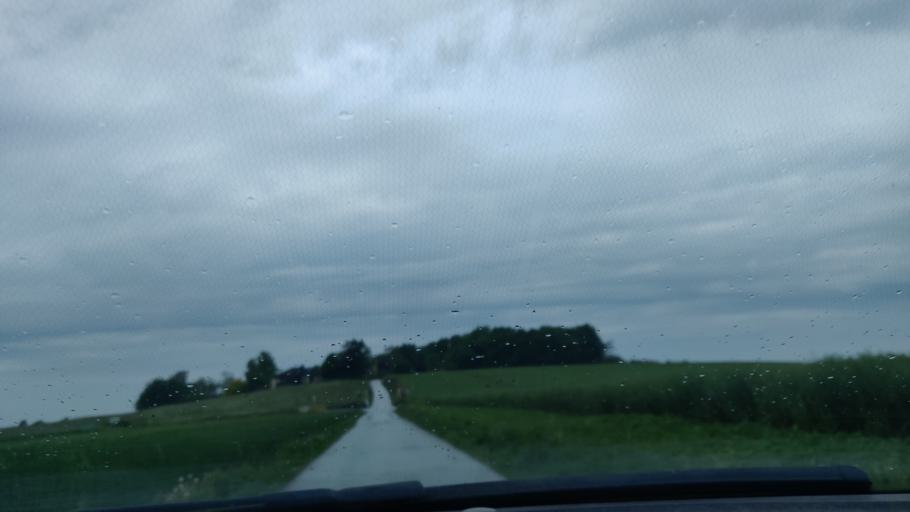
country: DE
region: North Rhine-Westphalia
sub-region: Regierungsbezirk Dusseldorf
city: Heiligenhaus
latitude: 51.3041
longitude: 6.9307
